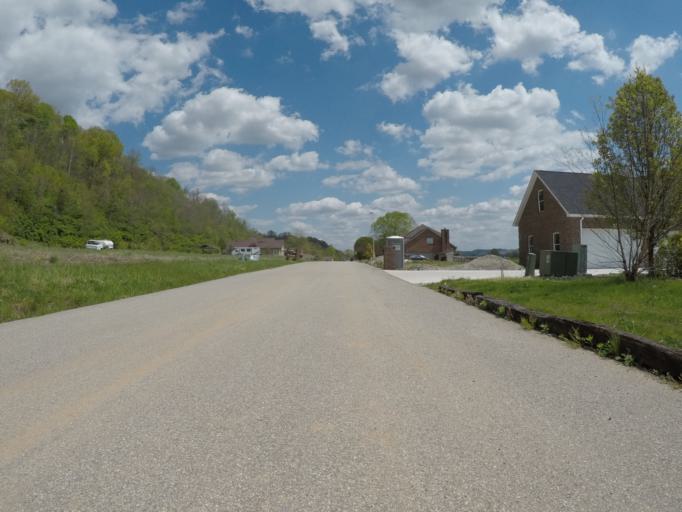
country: US
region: West Virginia
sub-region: Cabell County
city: Huntington
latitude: 38.4472
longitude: -82.3849
